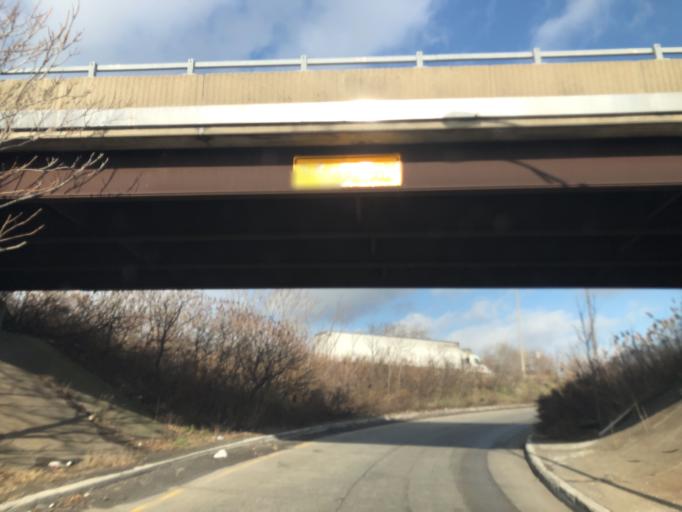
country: US
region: New Jersey
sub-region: Essex County
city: Newark
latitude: 40.7098
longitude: -74.1590
